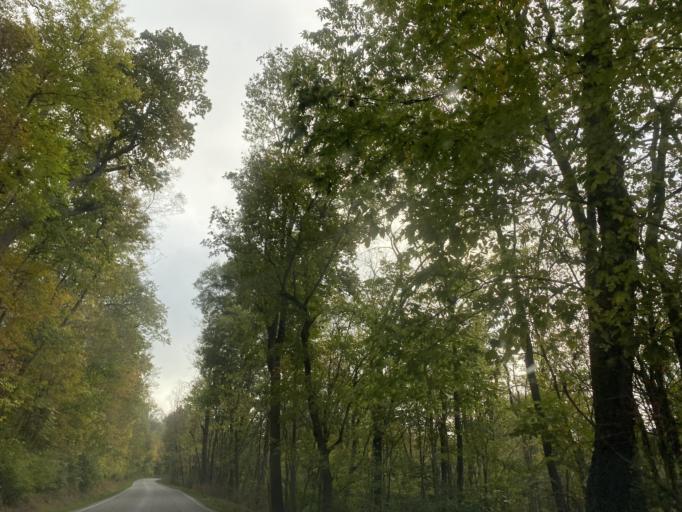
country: US
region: Kentucky
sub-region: Pendleton County
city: Falmouth
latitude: 38.7256
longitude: -84.3083
